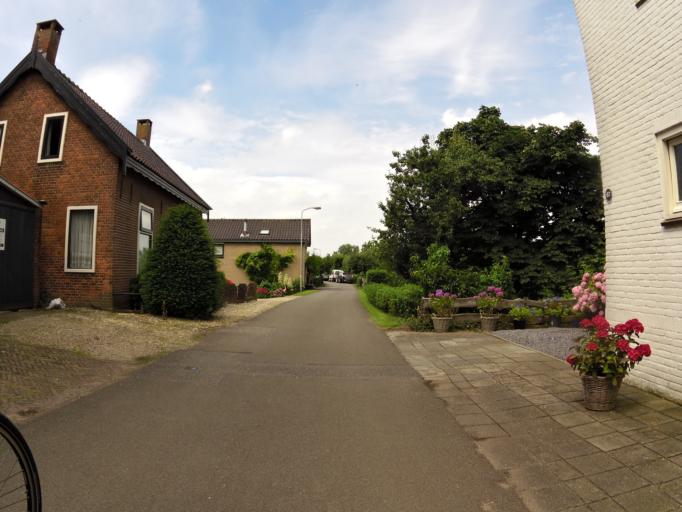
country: NL
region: South Holland
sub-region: Gemeente Leerdam
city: Leerdam
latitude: 51.8840
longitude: 5.1558
